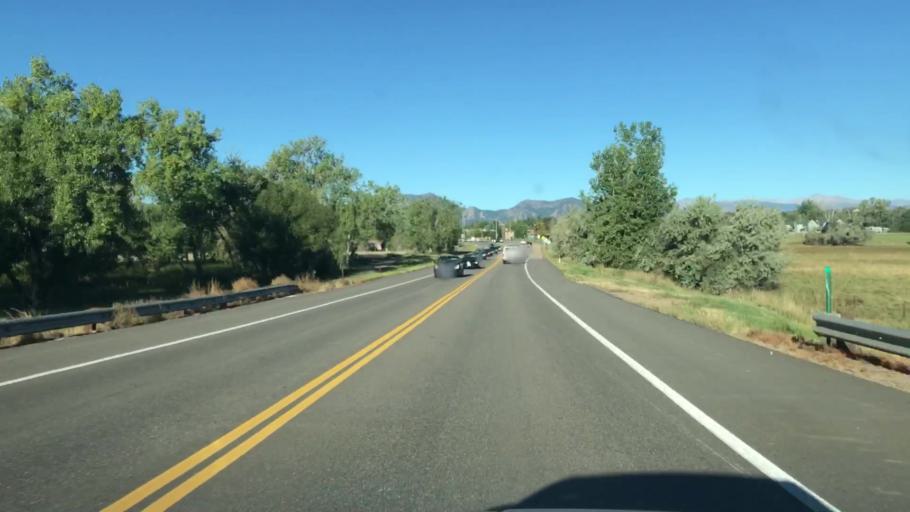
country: US
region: Colorado
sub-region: Boulder County
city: Louisville
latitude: 39.9726
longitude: -105.1218
